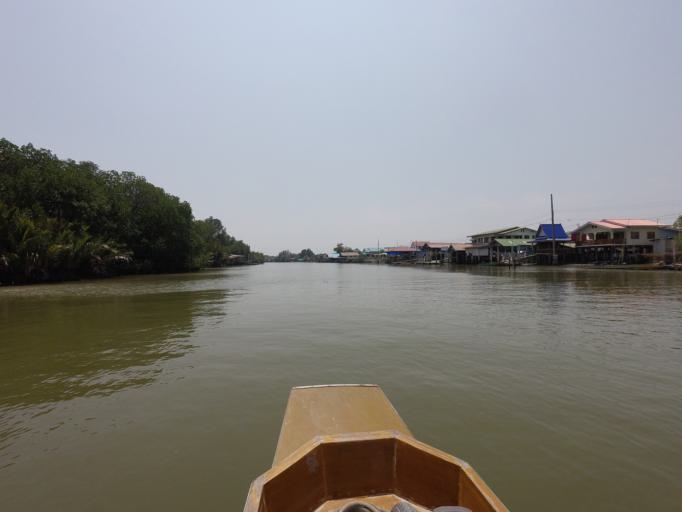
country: TH
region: Bangkok
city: Thung Khru
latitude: 13.5414
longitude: 100.4495
